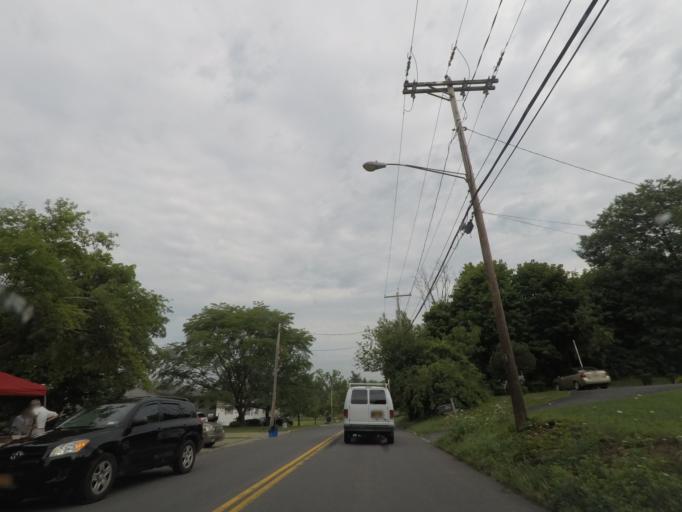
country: US
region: New York
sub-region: Saratoga County
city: Waterford
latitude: 42.7825
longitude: -73.6498
